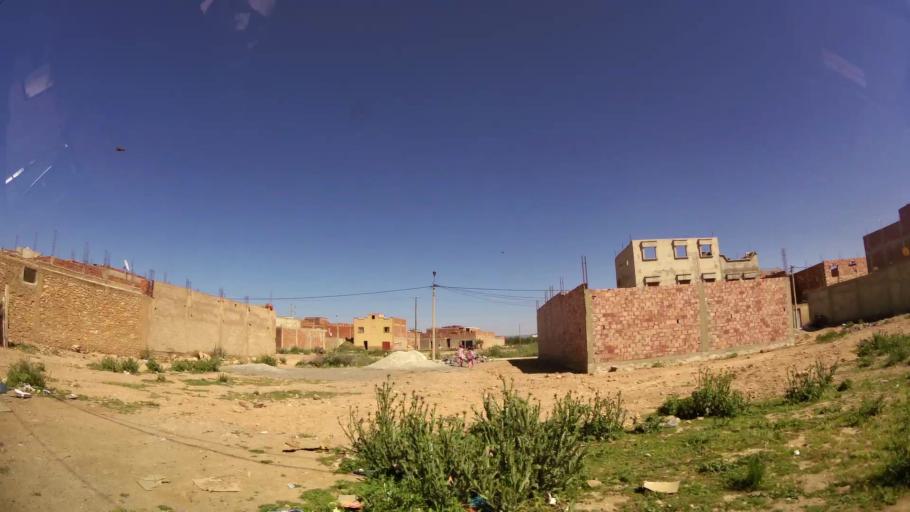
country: MA
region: Oriental
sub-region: Oujda-Angad
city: Oujda
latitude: 34.7226
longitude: -1.9028
